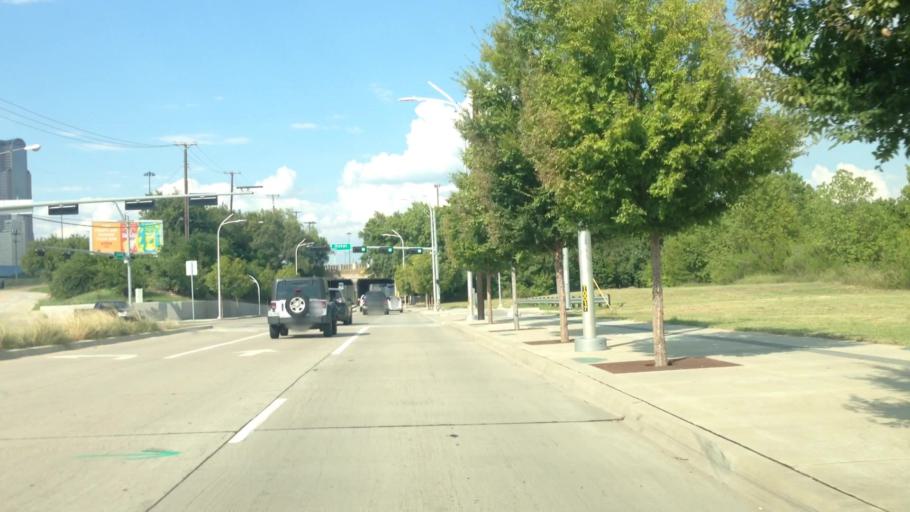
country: US
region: Texas
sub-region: Dallas County
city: Dallas
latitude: 32.7679
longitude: -96.8021
